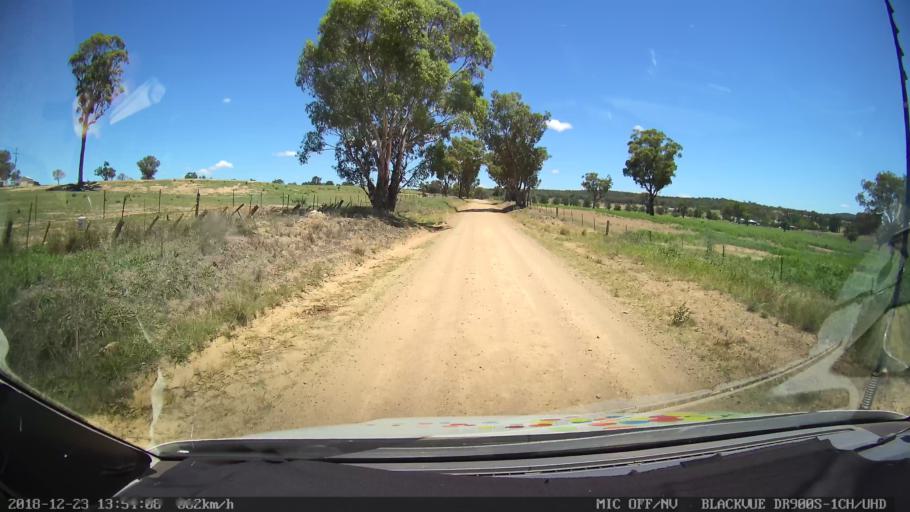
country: AU
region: New South Wales
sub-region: Tamworth Municipality
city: Manilla
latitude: -30.5582
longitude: 151.0912
